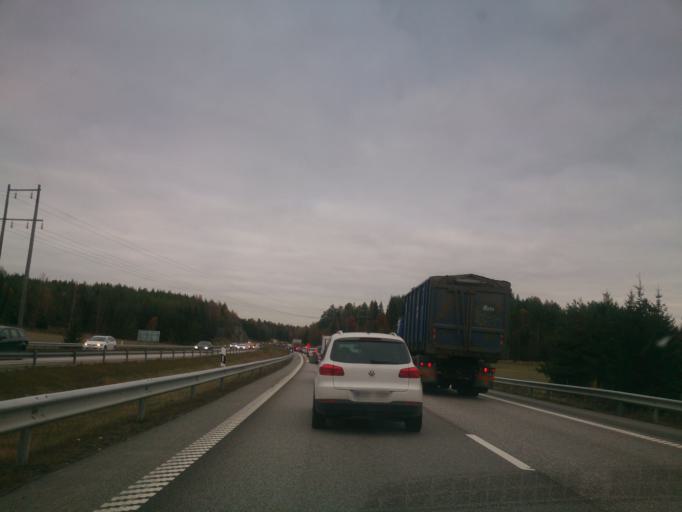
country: SE
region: Stockholm
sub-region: Sodertalje Kommun
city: Pershagen
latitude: 59.1056
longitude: 17.6098
